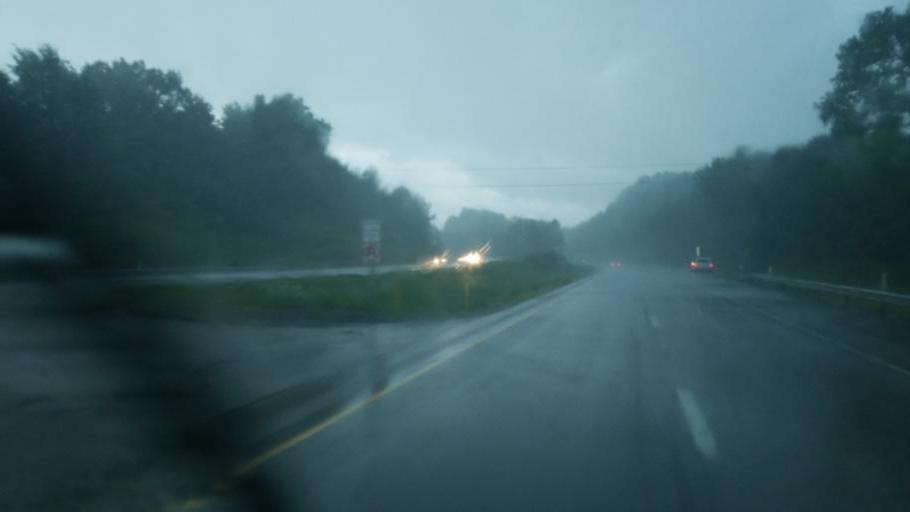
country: US
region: Pennsylvania
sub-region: Butler County
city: Prospect
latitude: 40.9002
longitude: -80.1231
